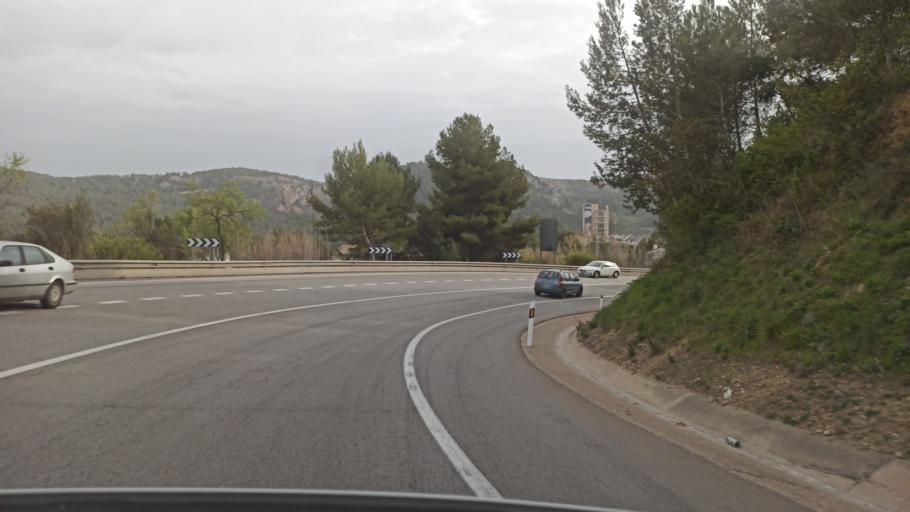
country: ES
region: Catalonia
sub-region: Provincia de Barcelona
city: Vallirana
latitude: 41.3818
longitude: 1.9115
